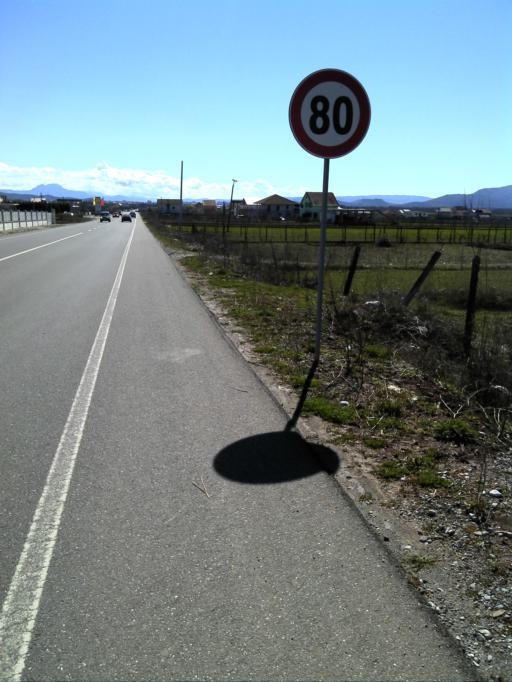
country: AL
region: Shkoder
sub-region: Rrethi i Malesia e Madhe
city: Grude-Fushe
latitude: 42.1317
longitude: 19.4899
